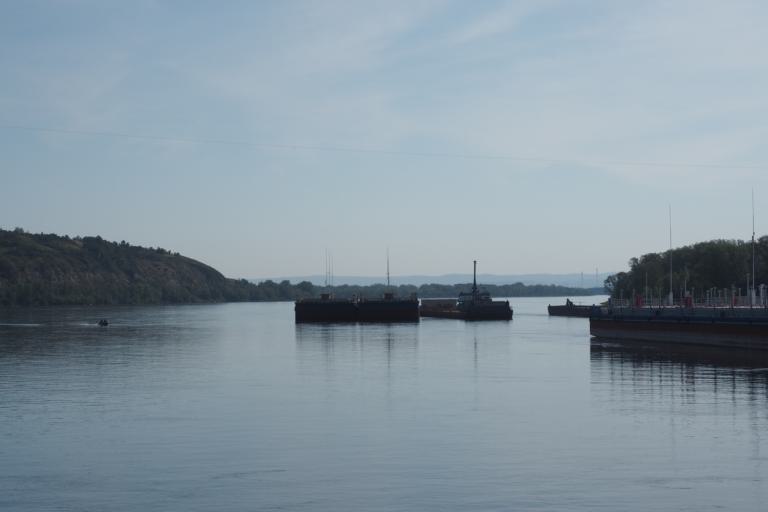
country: RU
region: Krasnoyarskiy
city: Berezovka
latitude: 56.1567
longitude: 93.1570
